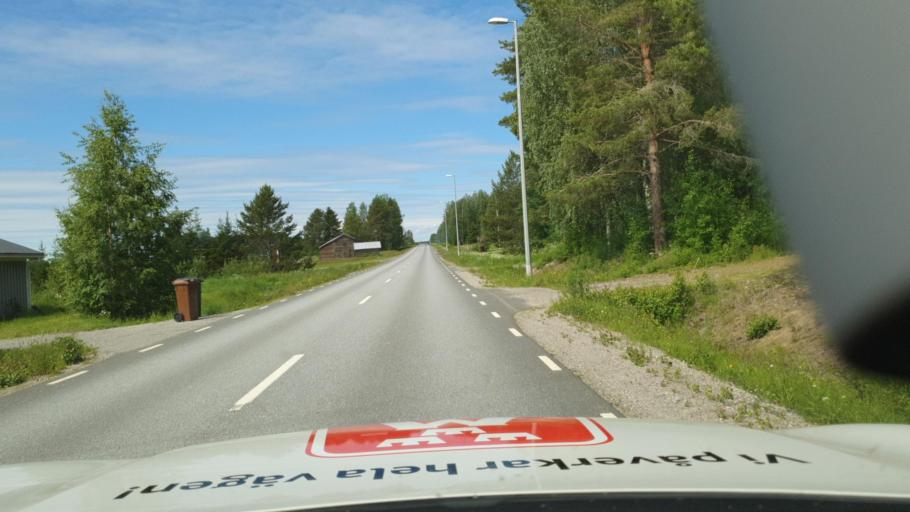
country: SE
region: Vaesterbotten
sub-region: Skelleftea Kommun
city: Forsbacka
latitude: 64.6998
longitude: 20.4681
